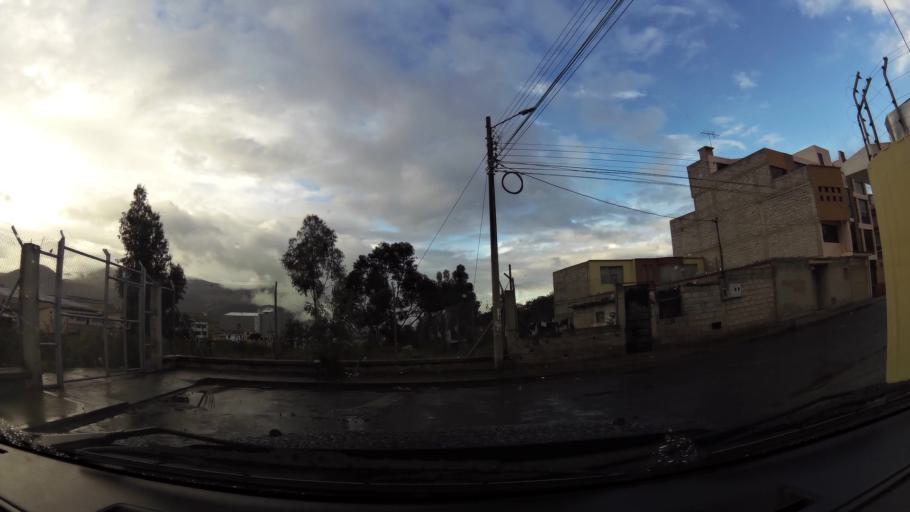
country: EC
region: Pichincha
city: Quito
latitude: -0.1059
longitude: -78.4896
